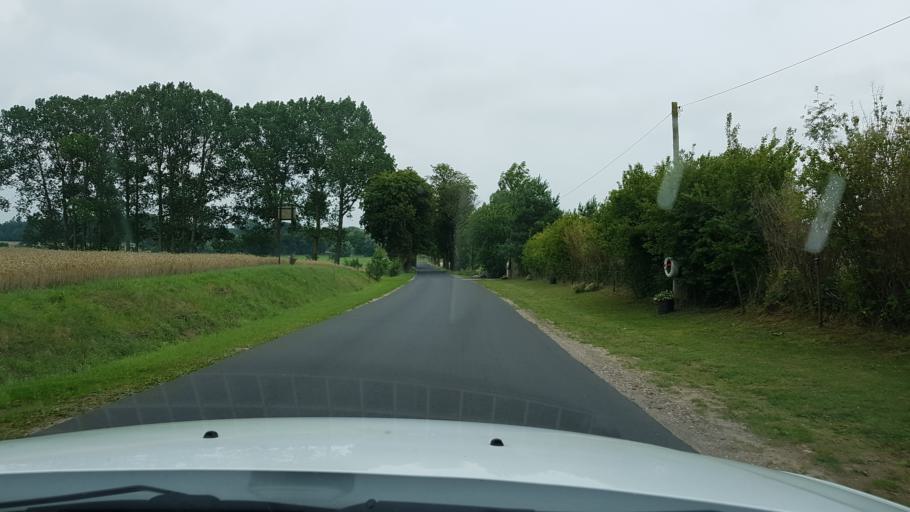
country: PL
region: West Pomeranian Voivodeship
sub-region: Powiat slawienski
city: Slawno
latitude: 54.4944
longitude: 16.5778
